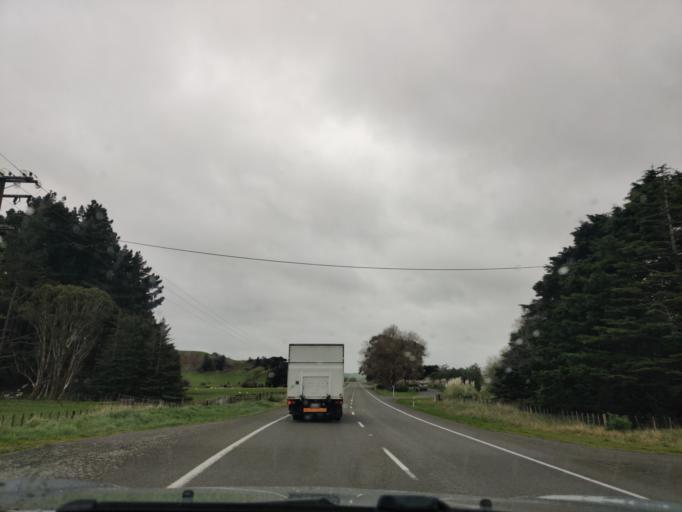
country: NZ
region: Manawatu-Wanganui
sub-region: Palmerston North City
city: Palmerston North
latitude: -40.3391
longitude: 175.8895
